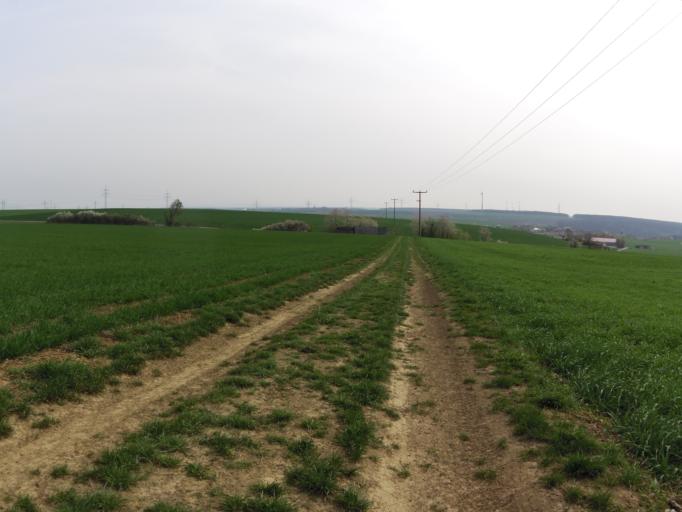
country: DE
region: Bavaria
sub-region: Regierungsbezirk Unterfranken
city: Theilheim
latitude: 49.7707
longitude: 10.0357
